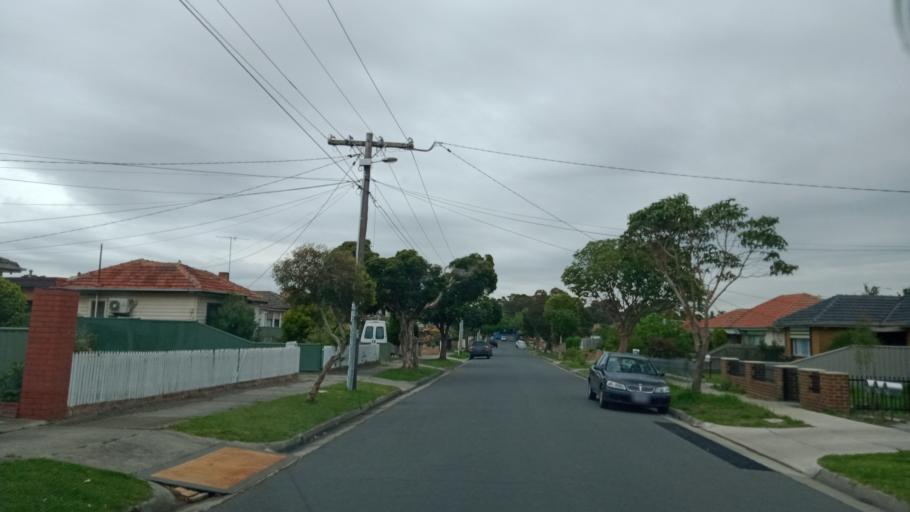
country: AU
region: Victoria
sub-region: Greater Dandenong
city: Springvale
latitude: -37.9471
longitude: 145.1568
